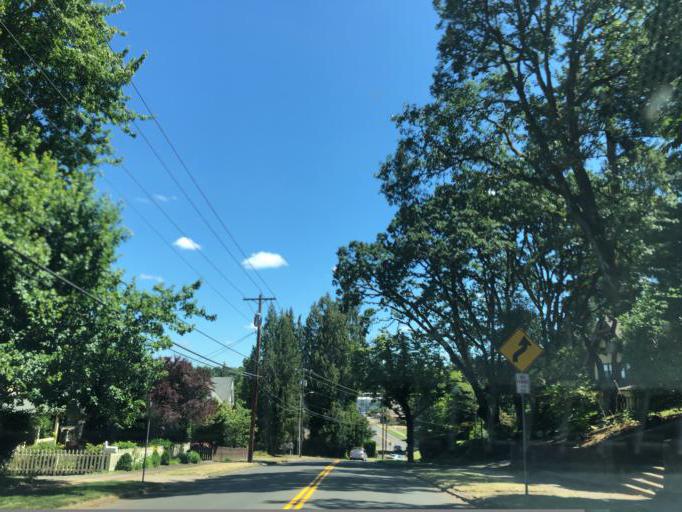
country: US
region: Oregon
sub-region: Marion County
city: Silverton
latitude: 45.0029
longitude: -122.7878
